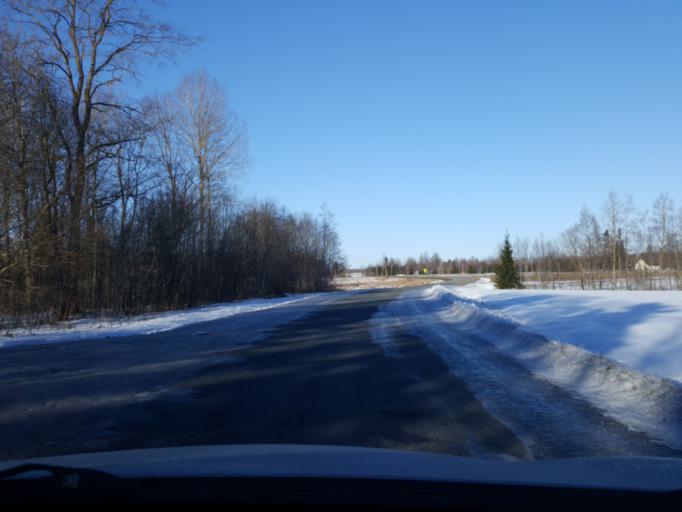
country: EE
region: Viljandimaa
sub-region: Viljandi linn
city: Viljandi
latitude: 58.4056
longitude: 25.5705
